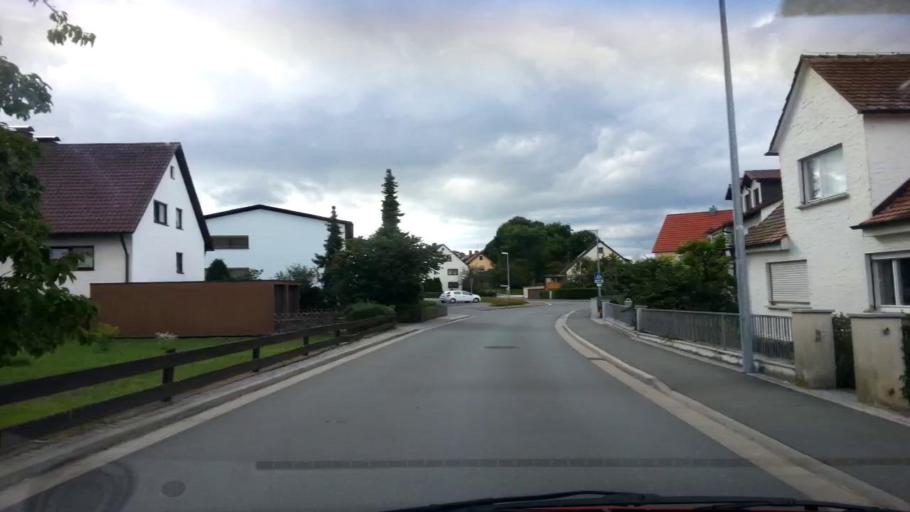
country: DE
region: Bavaria
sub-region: Upper Franconia
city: Heroldsbach
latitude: 49.6909
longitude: 10.9966
